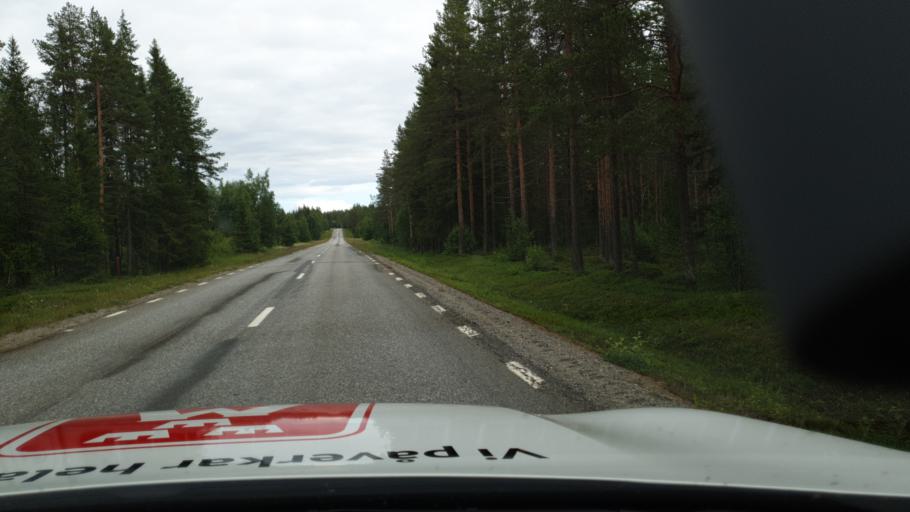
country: SE
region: Vaesterbotten
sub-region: Lycksele Kommun
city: Soderfors
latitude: 64.6182
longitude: 18.1591
